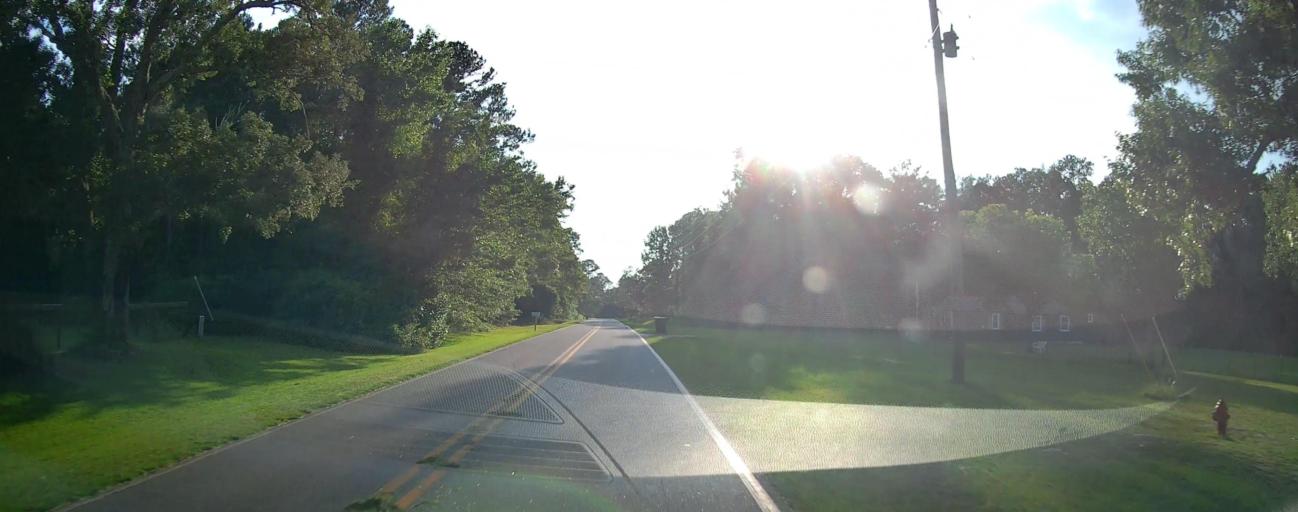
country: US
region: Georgia
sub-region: Peach County
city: Byron
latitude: 32.7055
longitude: -83.8296
